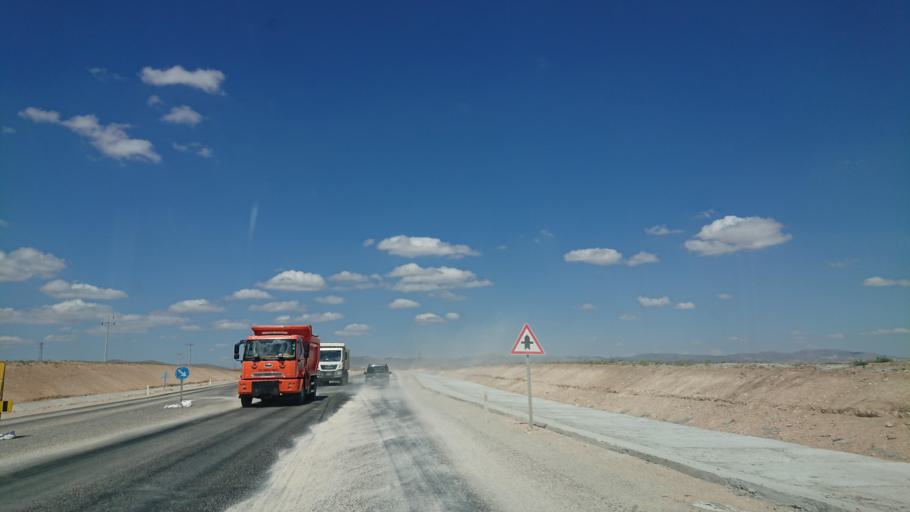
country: TR
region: Kirsehir
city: Kirsehir
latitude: 39.1308
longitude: 34.0399
